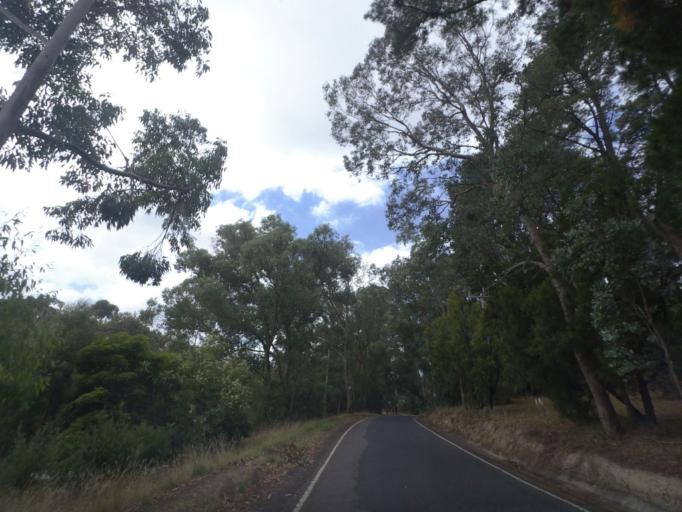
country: AU
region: Victoria
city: Mitcham
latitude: -37.7983
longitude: 145.2075
